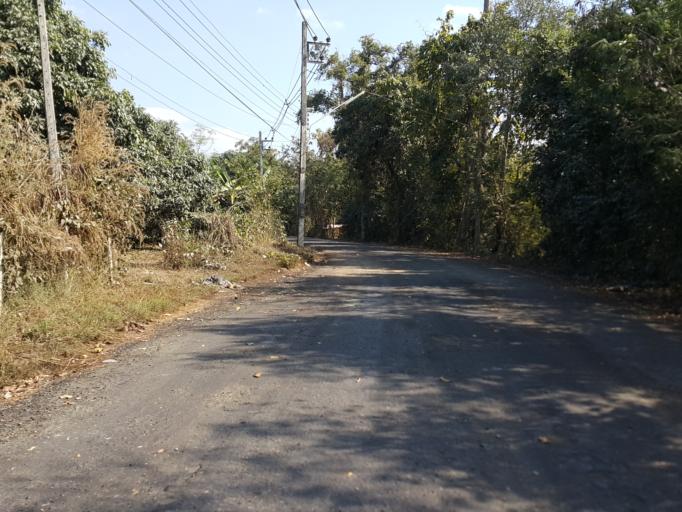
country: TH
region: Chiang Mai
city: Mae On
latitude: 18.8342
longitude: 99.2100
